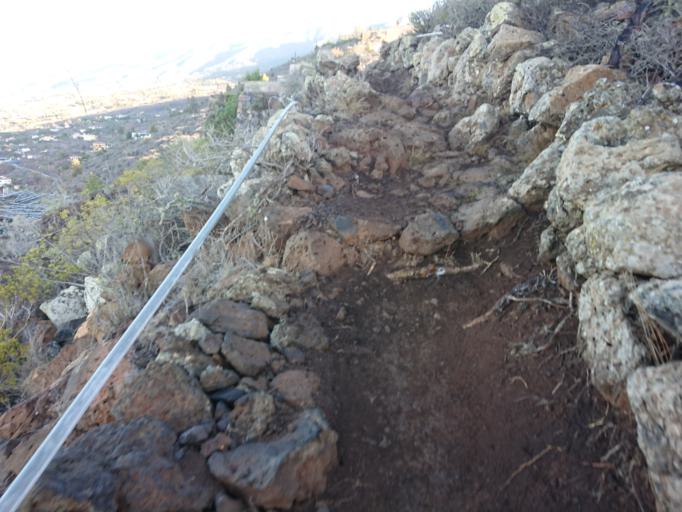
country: ES
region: Canary Islands
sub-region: Provincia de Santa Cruz de Tenerife
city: Los Llanos de Aridane
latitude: 28.6667
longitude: -17.9419
